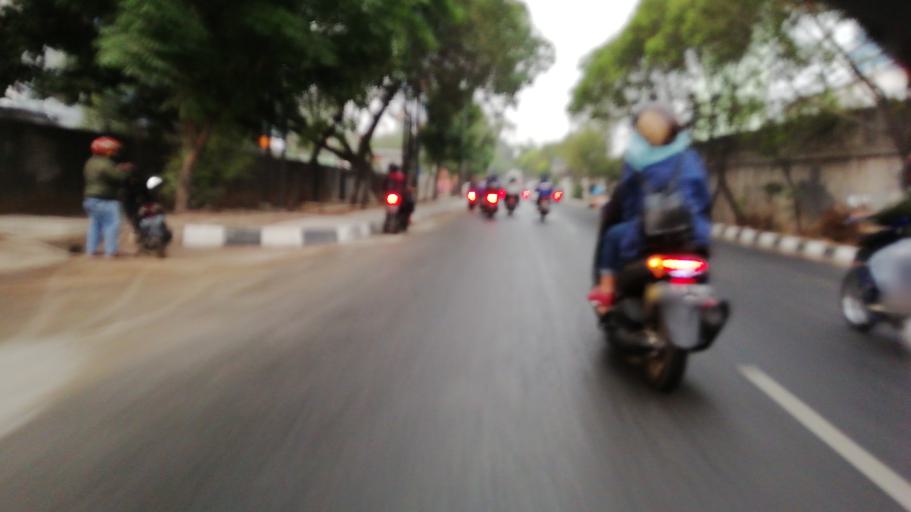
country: ID
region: Jakarta Raya
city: Jakarta
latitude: -6.2998
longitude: 106.8341
